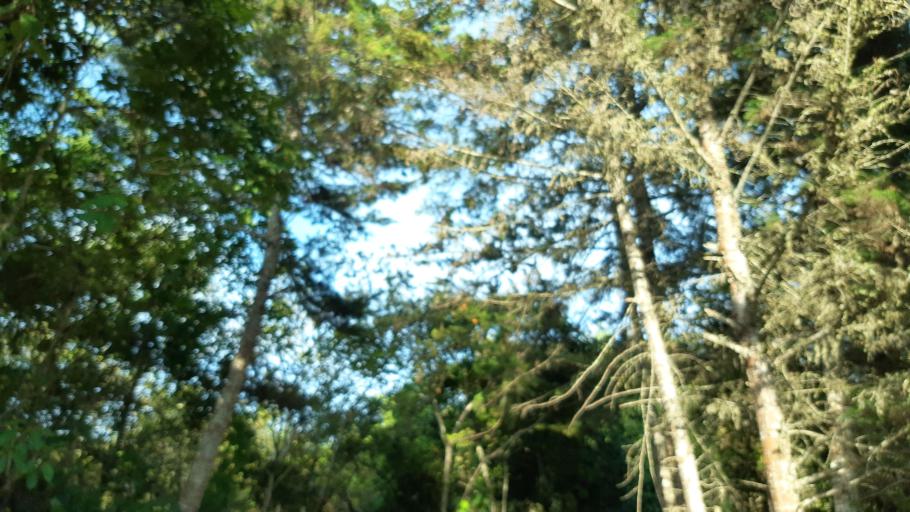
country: CO
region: Boyaca
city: Garagoa
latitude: 5.0682
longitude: -73.3760
